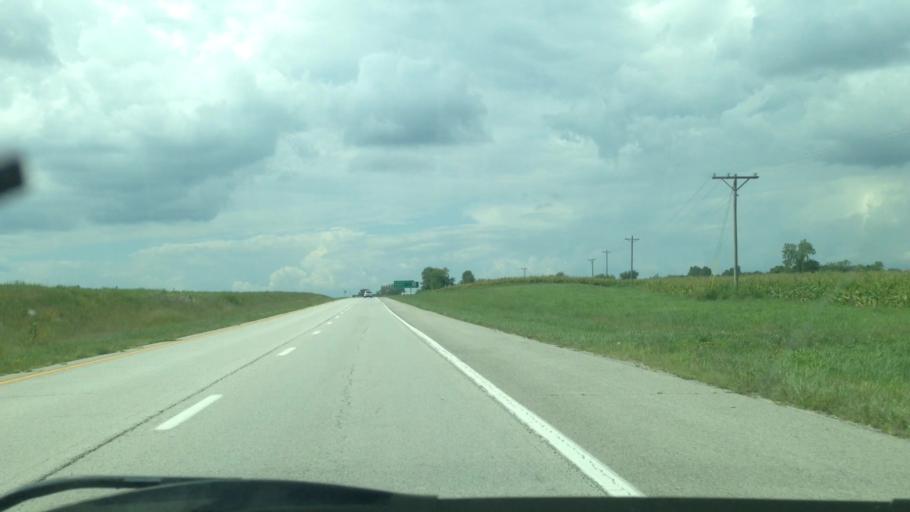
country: US
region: Missouri
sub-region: Pike County
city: Bowling Green
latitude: 39.2680
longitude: -91.0800
